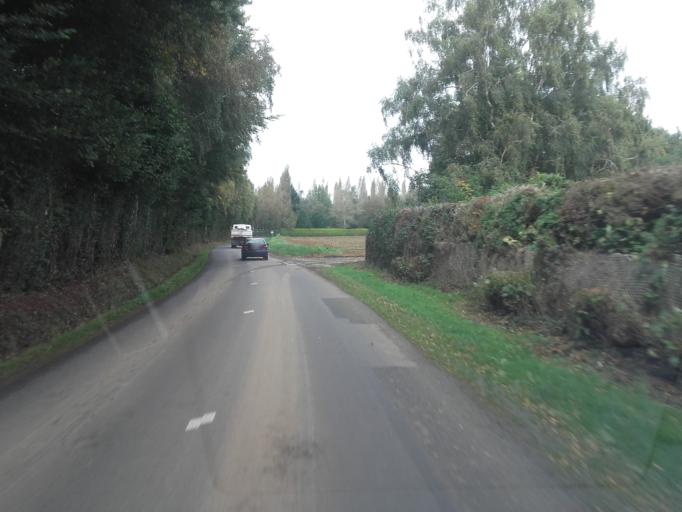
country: FR
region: Brittany
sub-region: Departement des Cotes-d'Armor
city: Plelo
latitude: 48.5794
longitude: -2.9481
